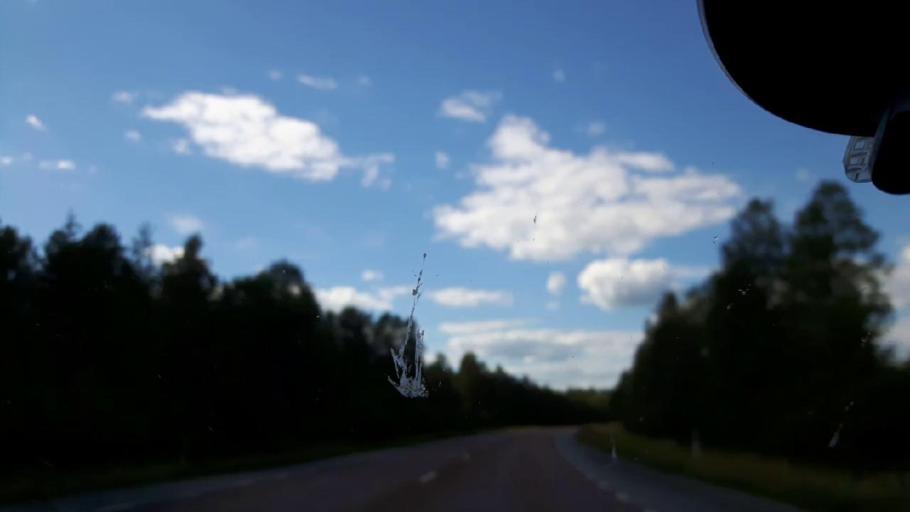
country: SE
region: Jaemtland
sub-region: Braecke Kommun
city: Braecke
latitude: 62.8191
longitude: 15.3351
